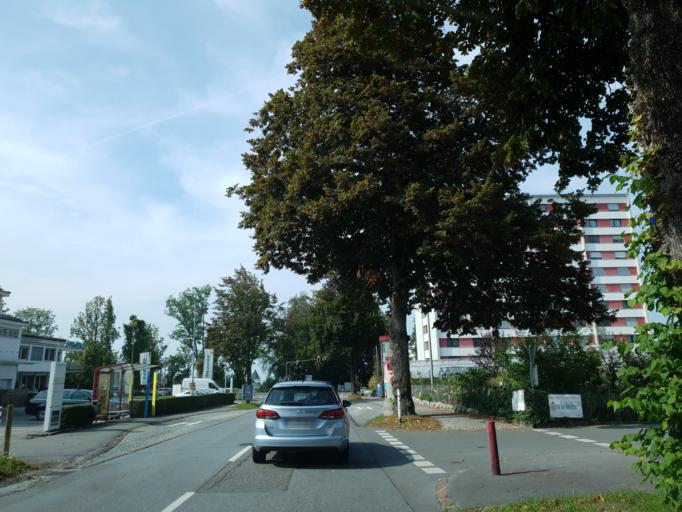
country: AT
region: Vorarlberg
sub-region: Politischer Bezirk Bregenz
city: Bregenz
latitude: 47.4967
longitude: 9.7356
